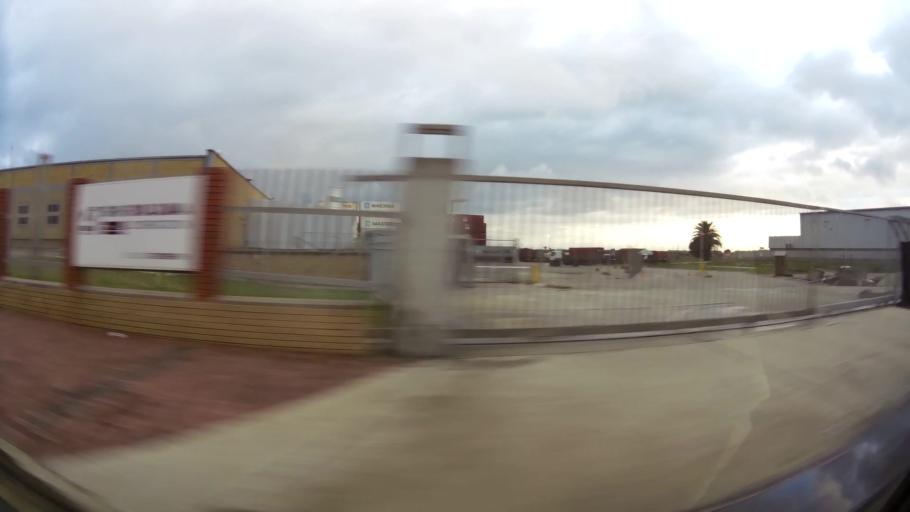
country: ZA
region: Eastern Cape
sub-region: Nelson Mandela Bay Metropolitan Municipality
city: Port Elizabeth
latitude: -33.9251
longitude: 25.5969
